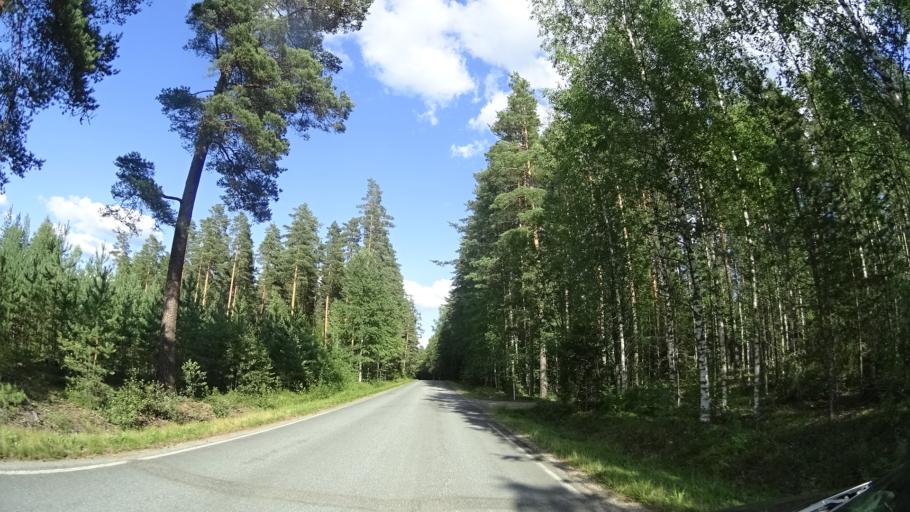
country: FI
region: Uusimaa
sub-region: Helsinki
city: Kaerkoelae
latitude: 60.7396
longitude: 24.1006
